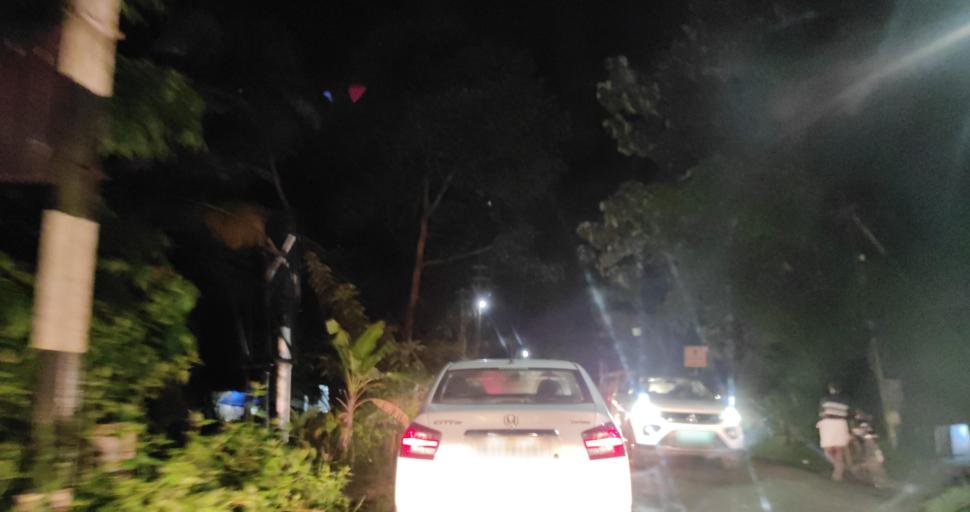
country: IN
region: Kerala
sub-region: Alappuzha
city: Vayalar
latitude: 9.7431
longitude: 76.3120
